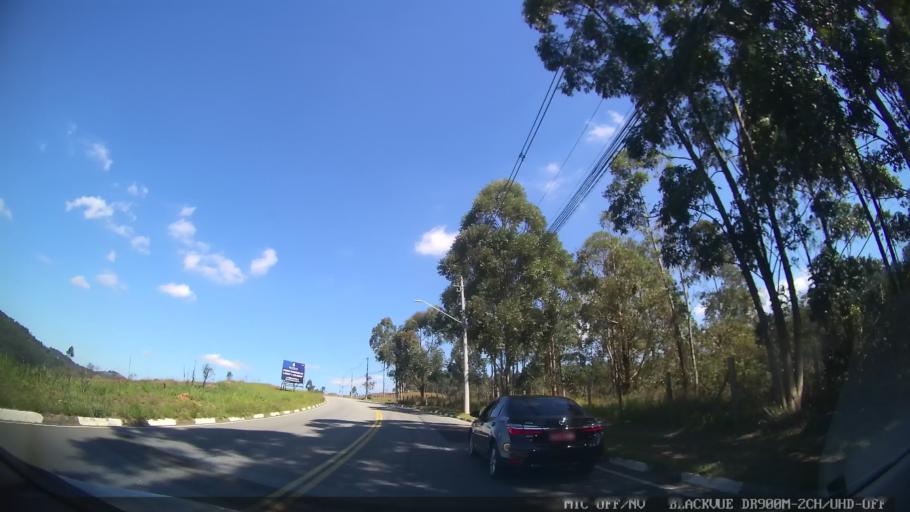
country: BR
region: Sao Paulo
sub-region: Barueri
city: Barueri
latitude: -23.4466
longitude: -46.8366
